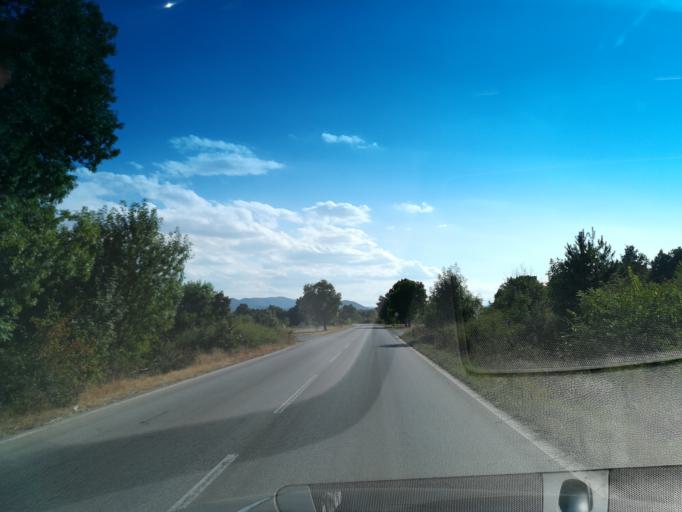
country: BG
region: Khaskovo
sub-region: Obshtina Mineralni Bani
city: Mineralni Bani
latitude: 41.9886
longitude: 25.3545
